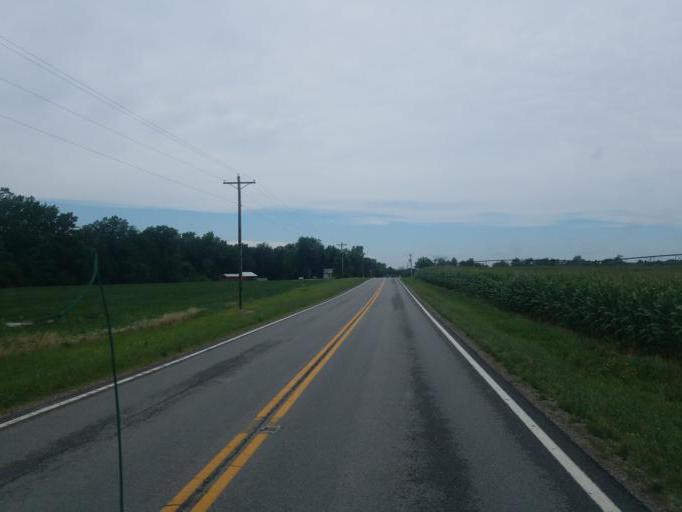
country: US
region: Ohio
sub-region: Williams County
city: Edgerton
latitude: 41.3834
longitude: -84.7962
